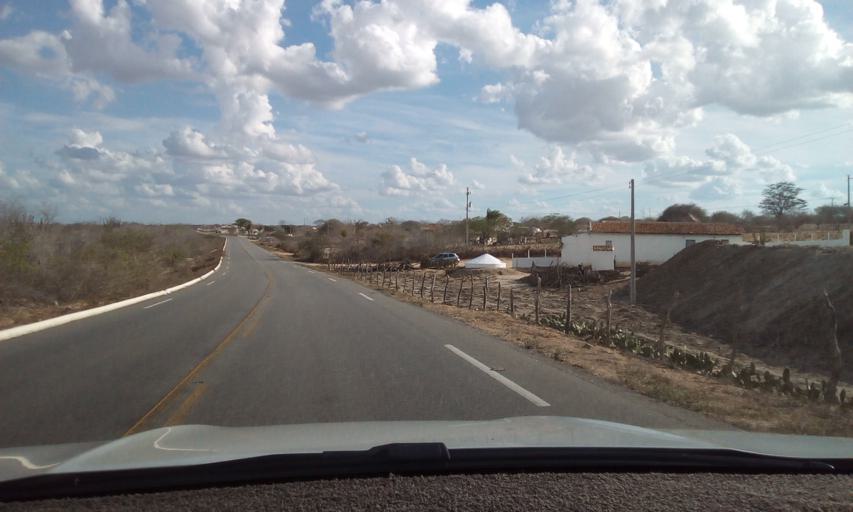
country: BR
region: Paraiba
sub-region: Soledade
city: Soledade
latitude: -6.8895
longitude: -36.3984
